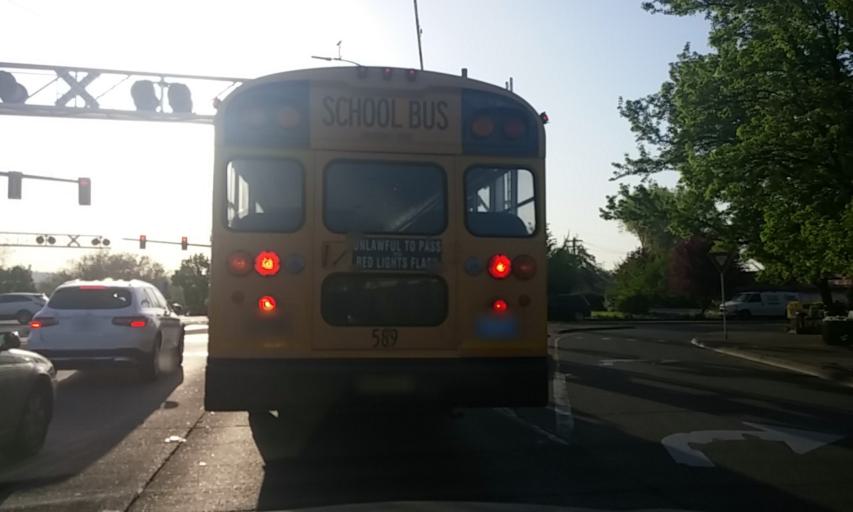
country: US
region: Oregon
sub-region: Washington County
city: Beaverton
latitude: 45.4865
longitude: -122.8009
